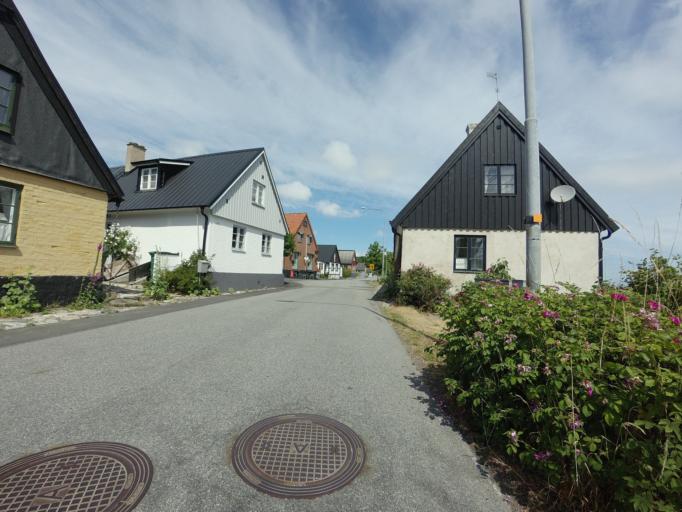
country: SE
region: Skane
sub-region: Simrishamns Kommun
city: Simrishamn
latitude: 55.5165
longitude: 14.3472
